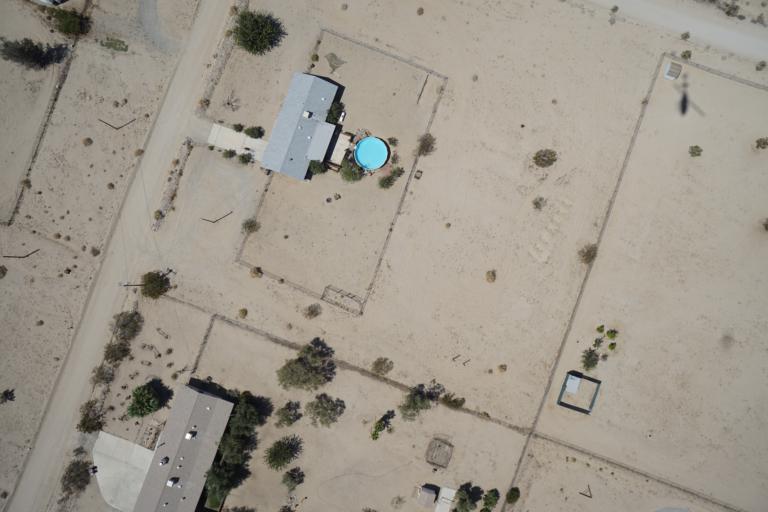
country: US
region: California
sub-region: San Bernardino County
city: Twentynine Palms
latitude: 34.1311
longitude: -116.0226
